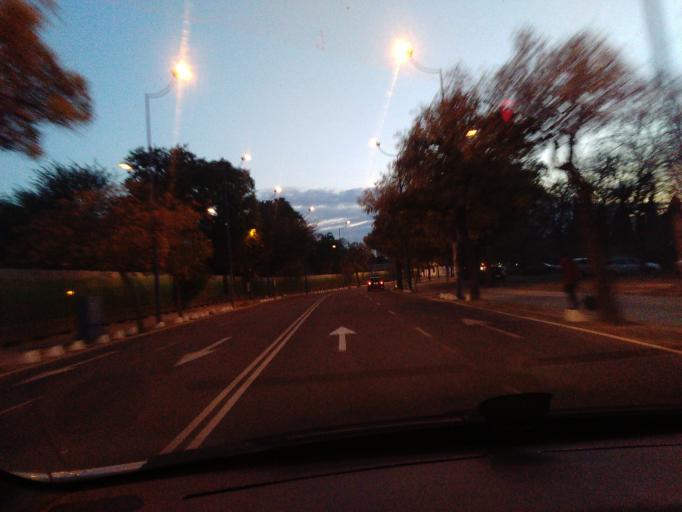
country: ES
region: Andalusia
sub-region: Provincia de Sevilla
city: Camas
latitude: 37.3993
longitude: -6.0049
